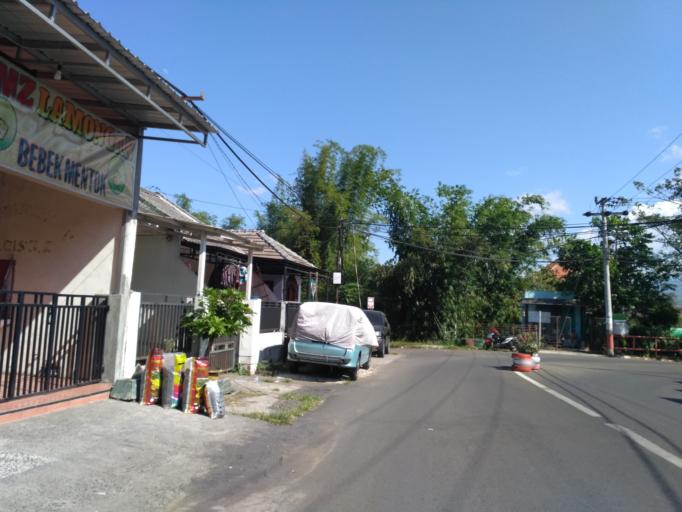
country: ID
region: East Java
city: Singosari
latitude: -7.9107
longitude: 112.6646
